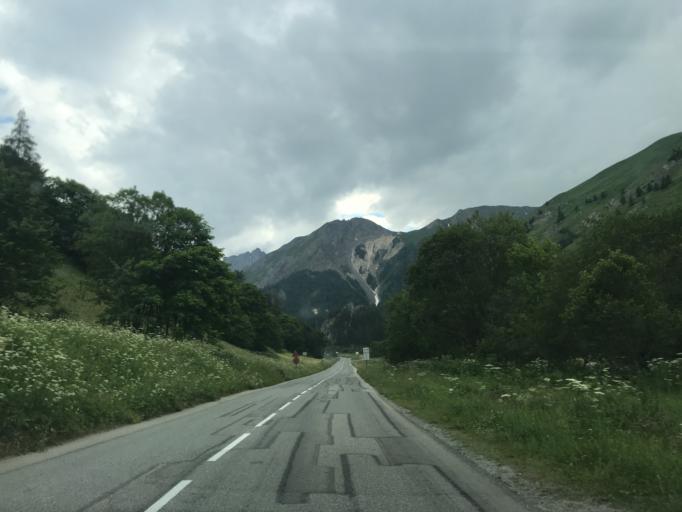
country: FR
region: Rhone-Alpes
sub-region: Departement de la Savoie
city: Valloire
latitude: 45.1360
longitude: 6.4197
